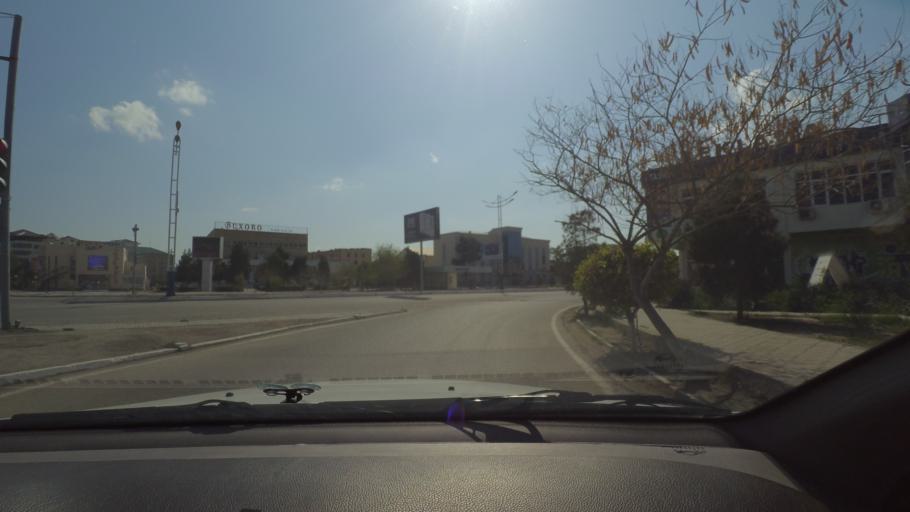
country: UZ
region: Bukhara
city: Bukhara
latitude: 39.7628
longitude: 64.4303
